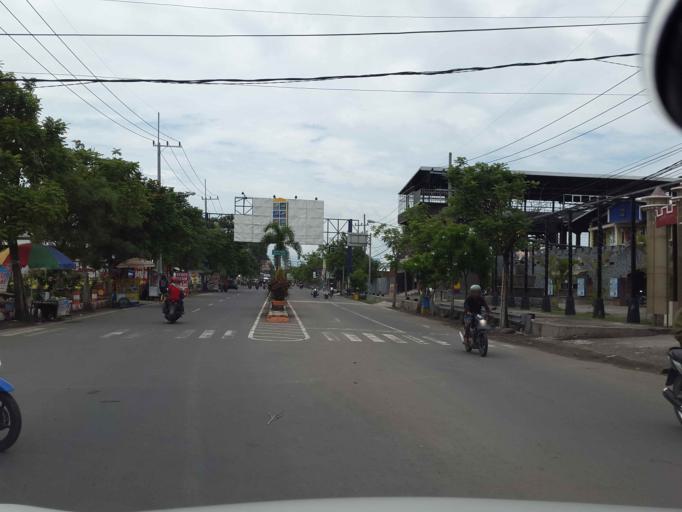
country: ID
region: East Java
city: Mojokerto
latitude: -7.4693
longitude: 112.4475
